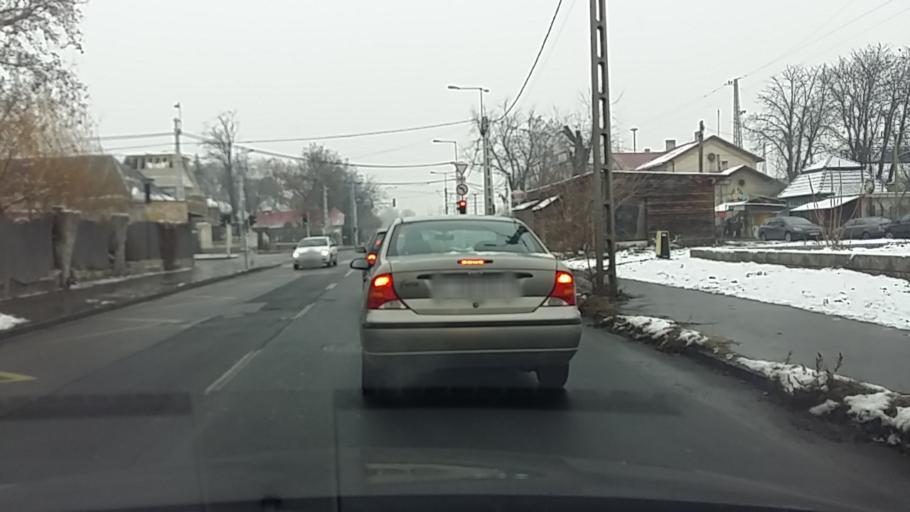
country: HU
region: Budapest
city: Budapest XV. keruelet
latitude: 47.5650
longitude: 19.1111
